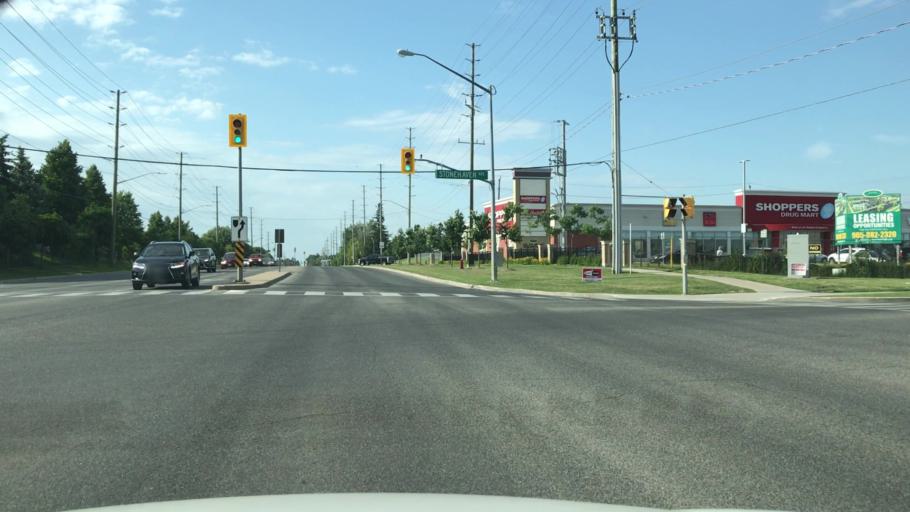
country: CA
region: Ontario
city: Newmarket
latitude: 44.0334
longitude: -79.4501
